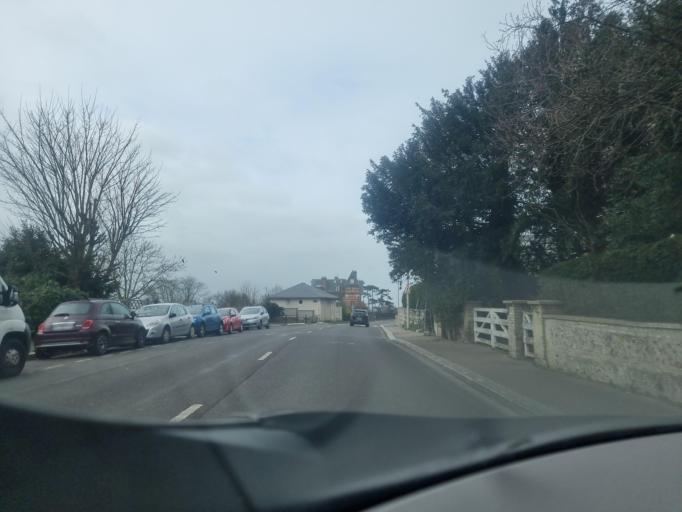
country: FR
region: Haute-Normandie
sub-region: Departement de la Seine-Maritime
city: Le Havre
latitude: 49.5001
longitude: 0.1035
